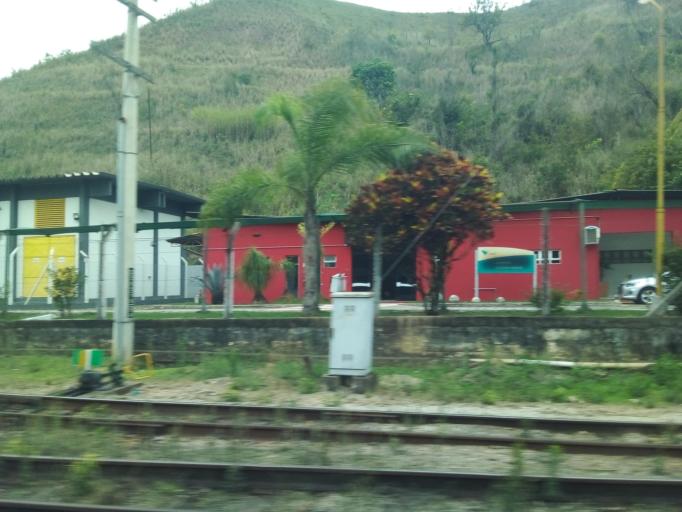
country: BR
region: Minas Gerais
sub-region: Nova Era
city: Nova Era
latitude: -19.7277
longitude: -43.0075
